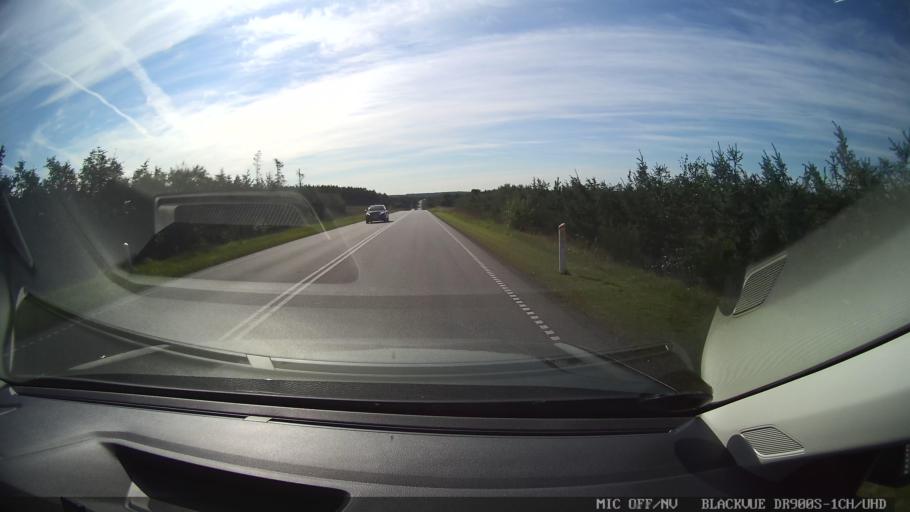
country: DK
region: North Denmark
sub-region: Mariagerfjord Kommune
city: Hadsund
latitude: 56.7637
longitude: 10.0654
